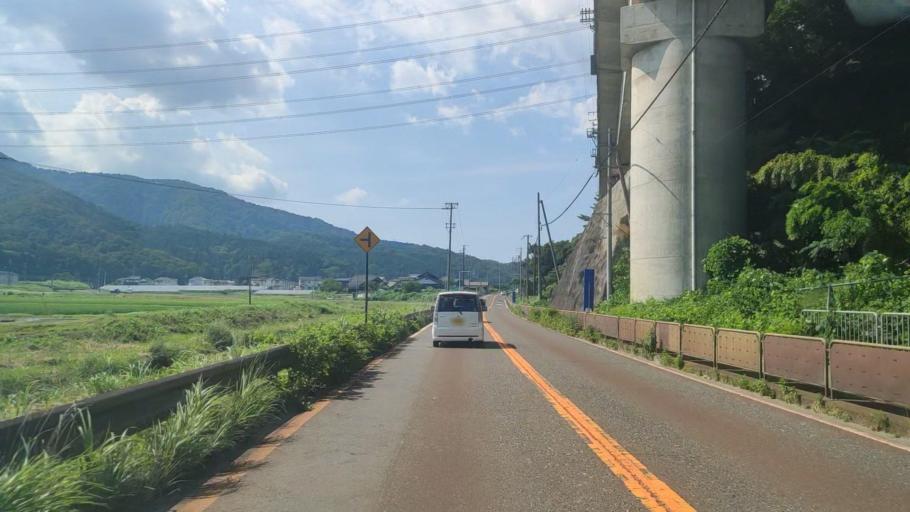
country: JP
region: Fukui
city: Tsuruga
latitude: 35.5321
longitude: 136.1545
